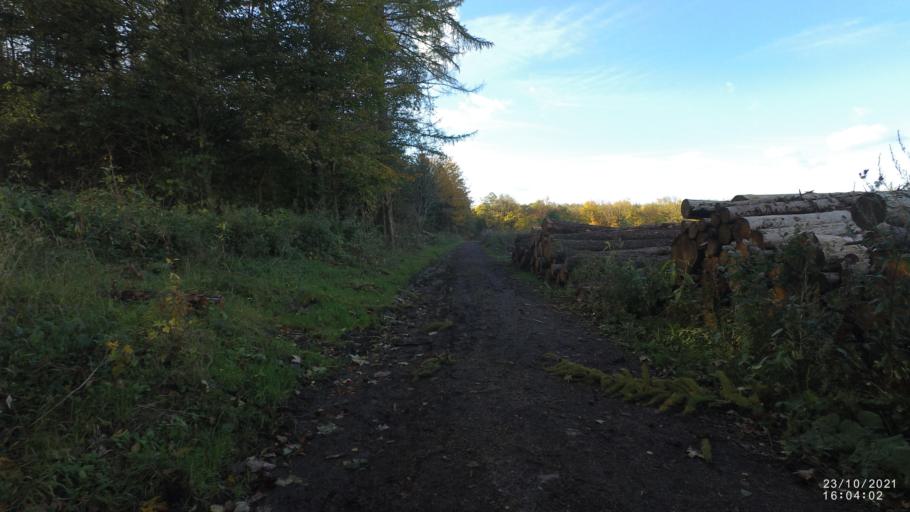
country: DE
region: North Rhine-Westphalia
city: Balve
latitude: 51.3712
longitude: 7.8491
